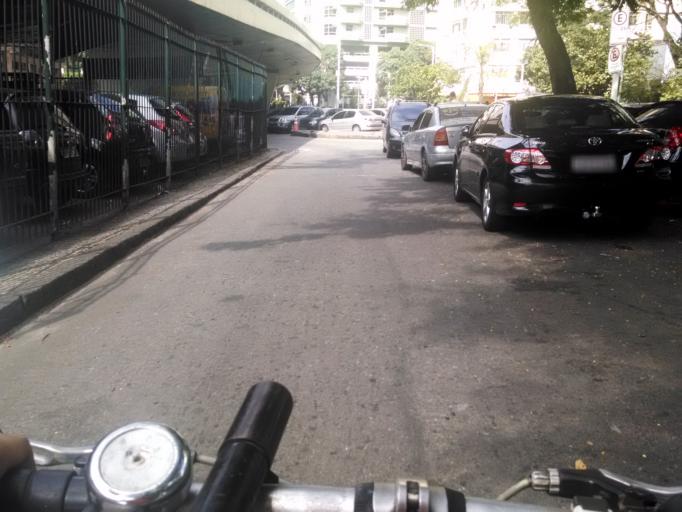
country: BR
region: Rio de Janeiro
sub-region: Rio De Janeiro
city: Rio de Janeiro
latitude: -22.9498
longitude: -43.1819
